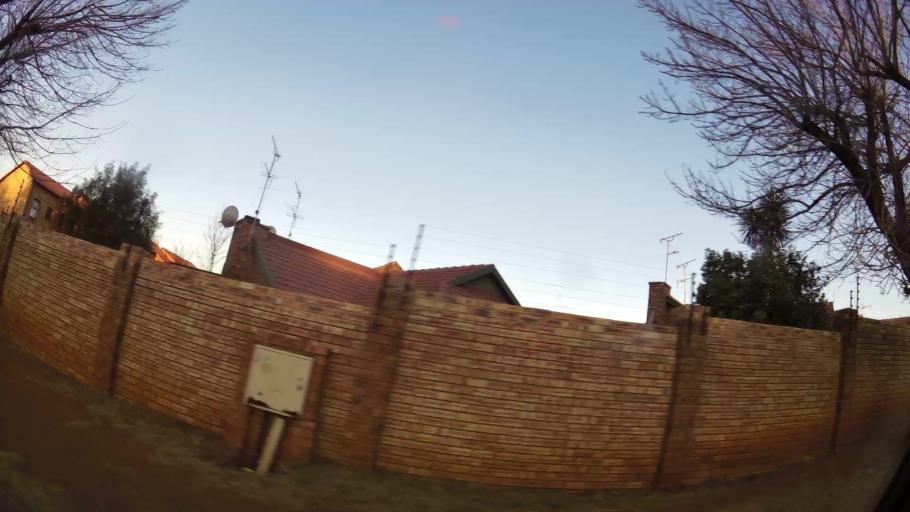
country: ZA
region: Gauteng
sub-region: Ekurhuleni Metropolitan Municipality
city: Germiston
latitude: -26.2578
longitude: 28.1652
